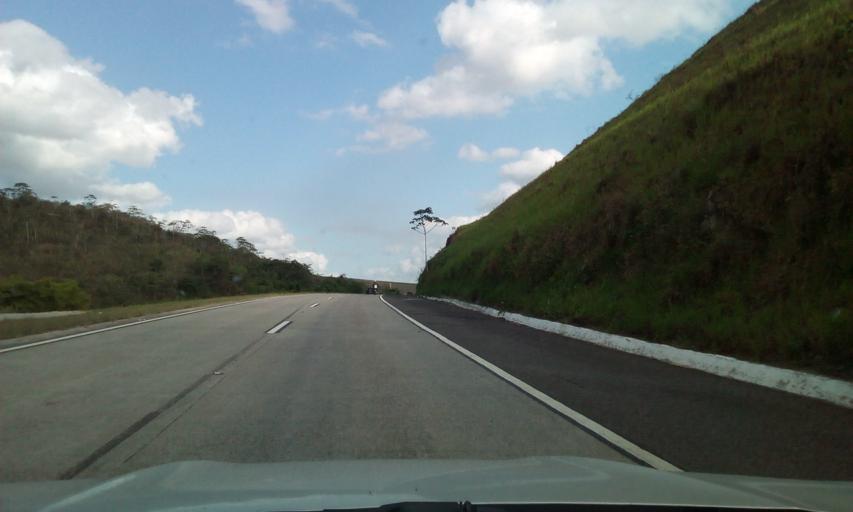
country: BR
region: Pernambuco
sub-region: Gameleira
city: Gameleira
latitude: -8.5509
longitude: -35.4404
